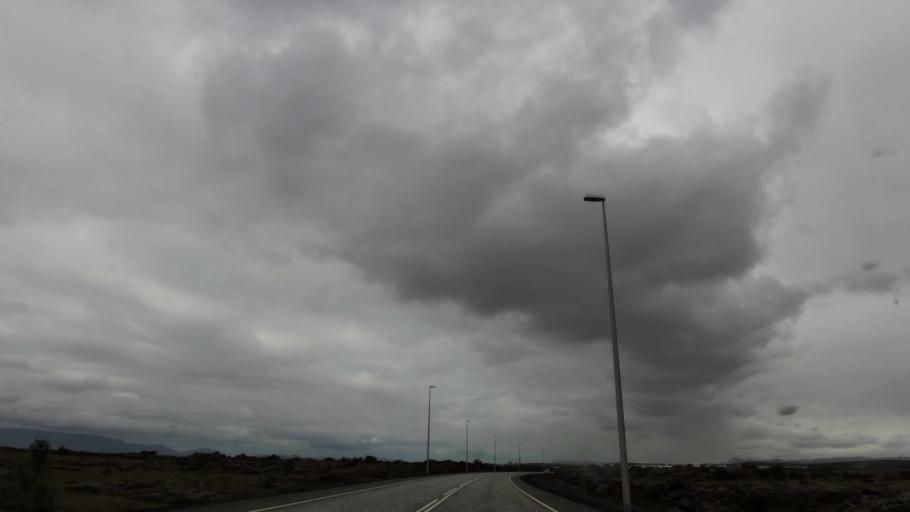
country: IS
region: Capital Region
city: Alftanes
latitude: 64.0907
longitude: -21.9758
